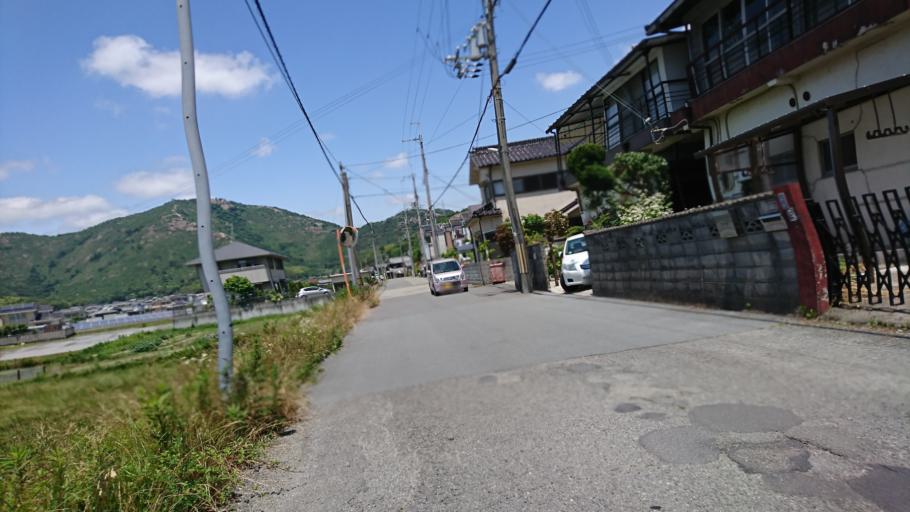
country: JP
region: Hyogo
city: Kakogawacho-honmachi
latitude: 34.7986
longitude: 134.7886
